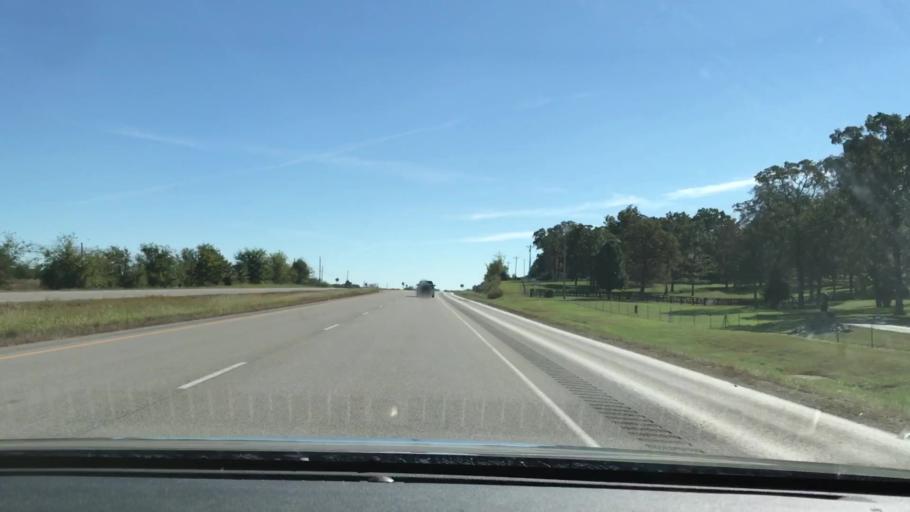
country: US
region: Kentucky
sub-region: Christian County
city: Hopkinsville
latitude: 36.8493
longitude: -87.3446
